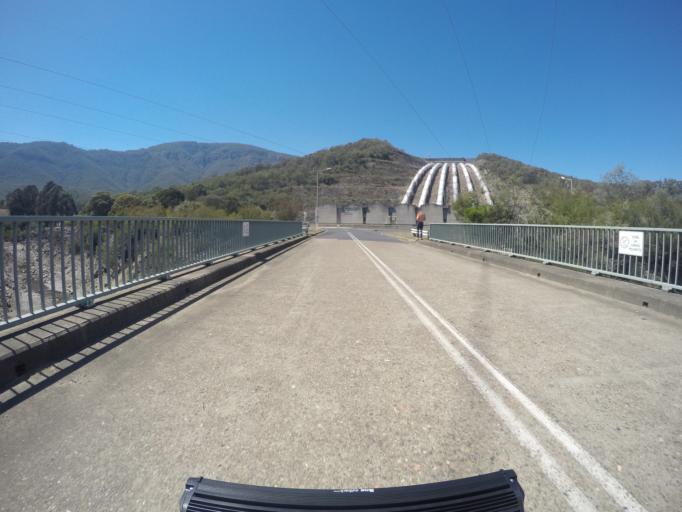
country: AU
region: New South Wales
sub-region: Tumut Shire
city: Tumut
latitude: -35.6095
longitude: 148.2901
